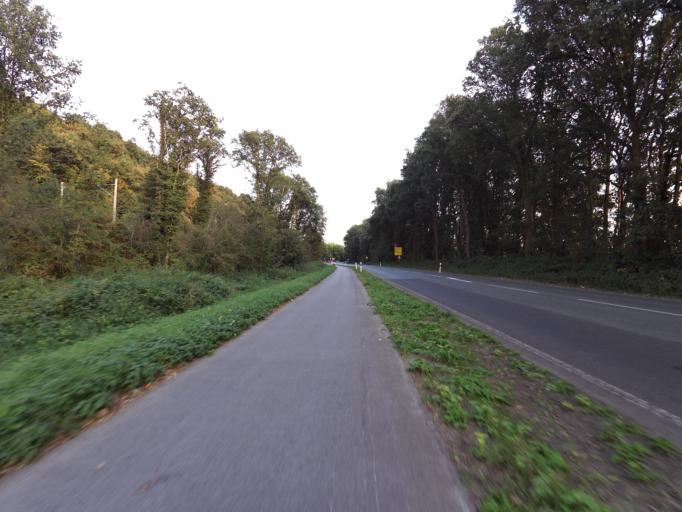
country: DE
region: North Rhine-Westphalia
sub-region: Regierungsbezirk Dusseldorf
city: Kleve
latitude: 51.8633
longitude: 6.1623
